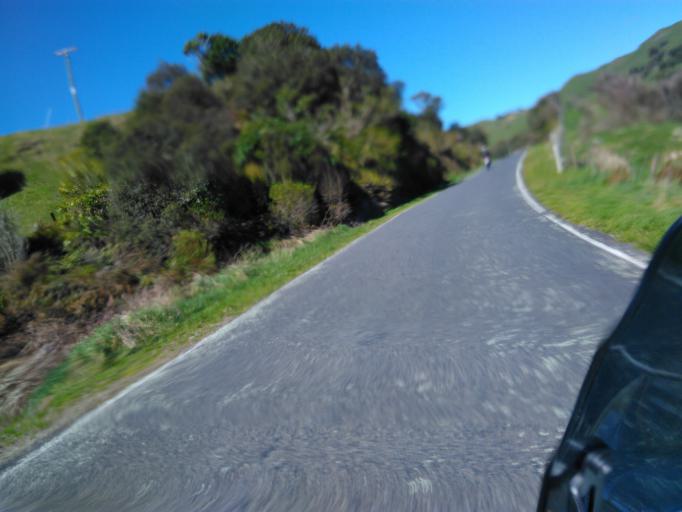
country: NZ
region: Bay of Plenty
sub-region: Opotiki District
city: Opotiki
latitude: -38.3213
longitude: 177.5319
